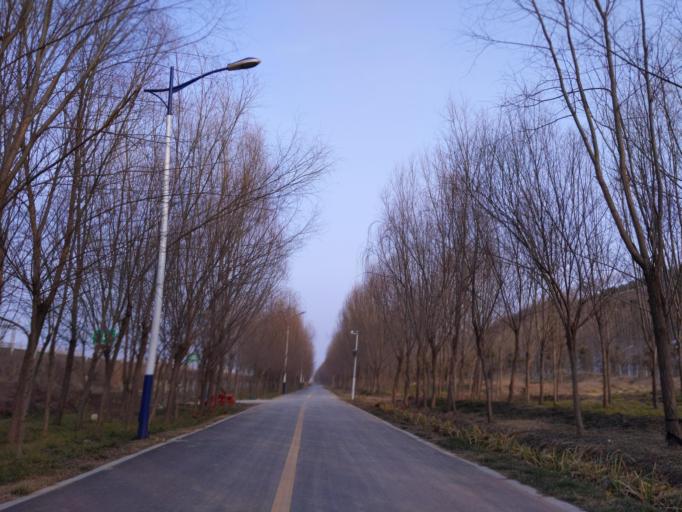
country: CN
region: Henan Sheng
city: Puyang
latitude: 35.8211
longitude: 115.0047
